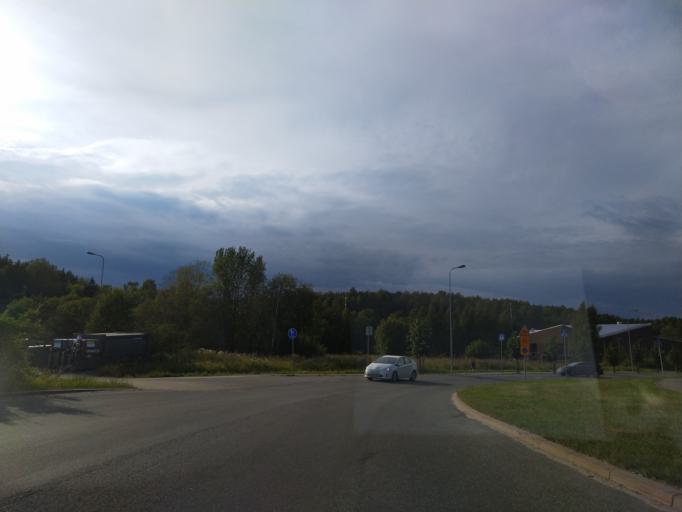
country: FI
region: Varsinais-Suomi
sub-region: Turku
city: Turku
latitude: 60.4180
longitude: 22.2293
